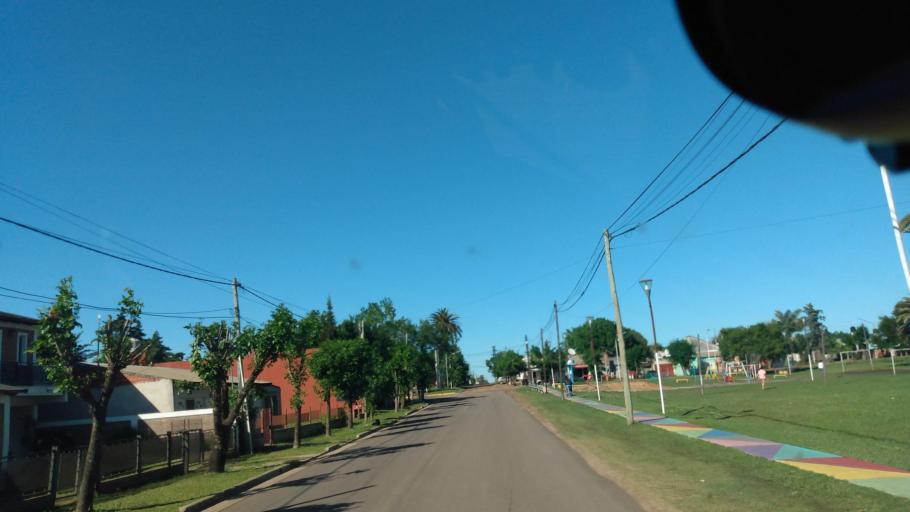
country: AR
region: Entre Rios
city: Colon
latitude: -32.1569
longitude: -58.1975
